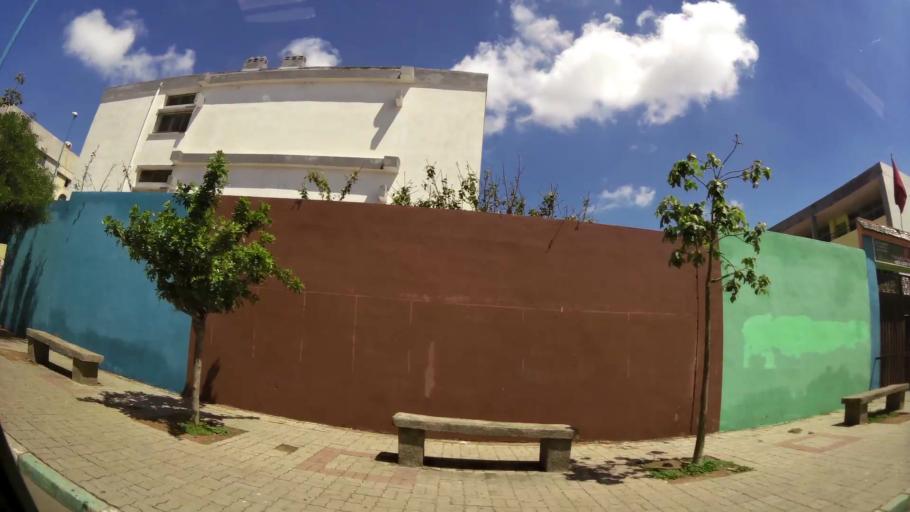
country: MA
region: Grand Casablanca
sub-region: Casablanca
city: Casablanca
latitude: 33.5648
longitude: -7.5727
